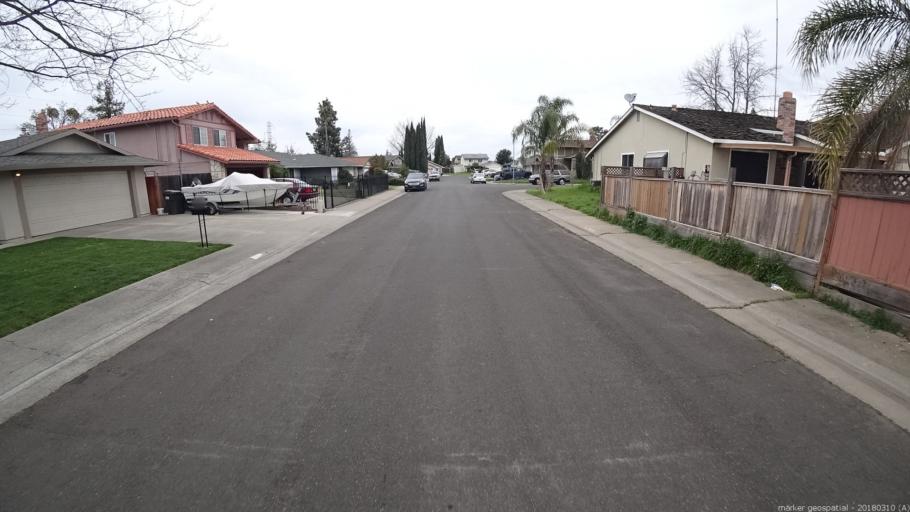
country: US
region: California
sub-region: Sacramento County
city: Florin
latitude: 38.4860
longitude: -121.4074
